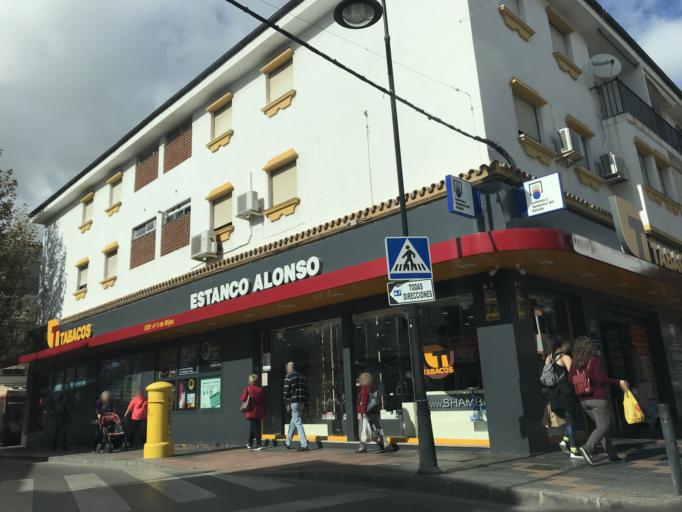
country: ES
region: Andalusia
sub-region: Provincia de Malaga
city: Fuengirola
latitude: 36.5404
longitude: -4.6306
